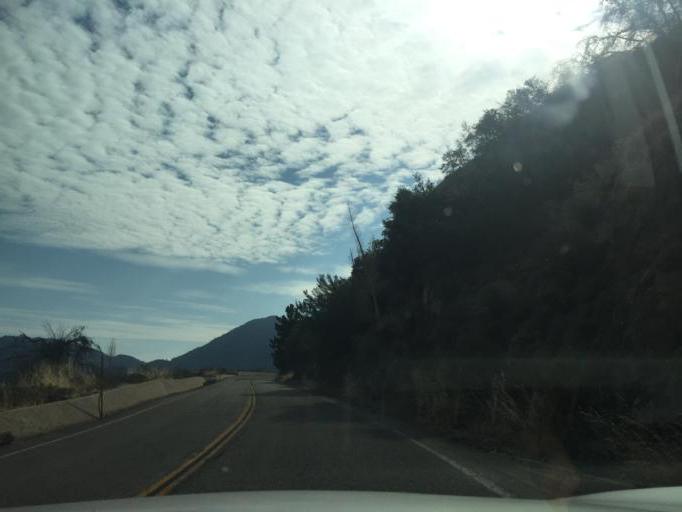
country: US
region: California
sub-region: Los Angeles County
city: Altadena
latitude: 34.2695
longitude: -118.0759
